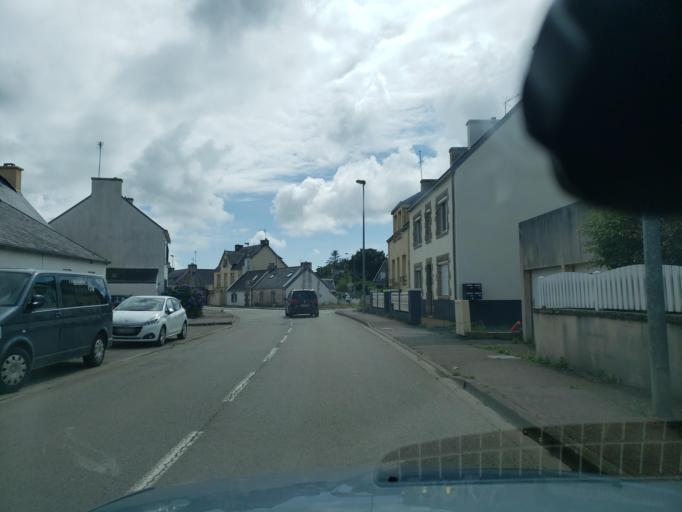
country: FR
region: Brittany
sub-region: Departement du Finistere
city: Ploneour-Lanvern
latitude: 47.9067
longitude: -4.2813
